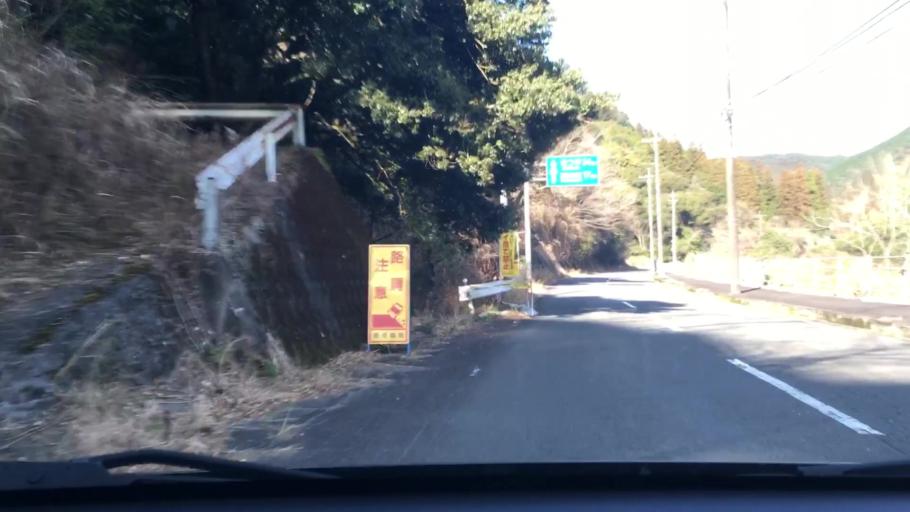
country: JP
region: Kagoshima
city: Ijuin
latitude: 31.7450
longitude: 130.4091
